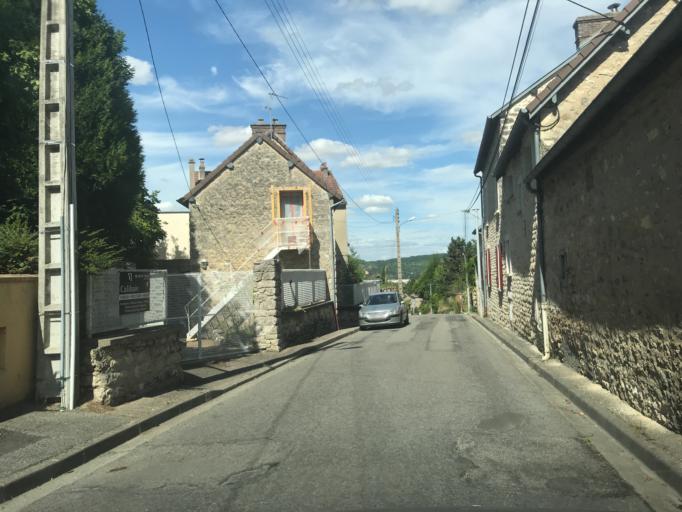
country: FR
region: Haute-Normandie
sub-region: Departement de l'Eure
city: Vernon
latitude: 49.0902
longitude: 1.4537
